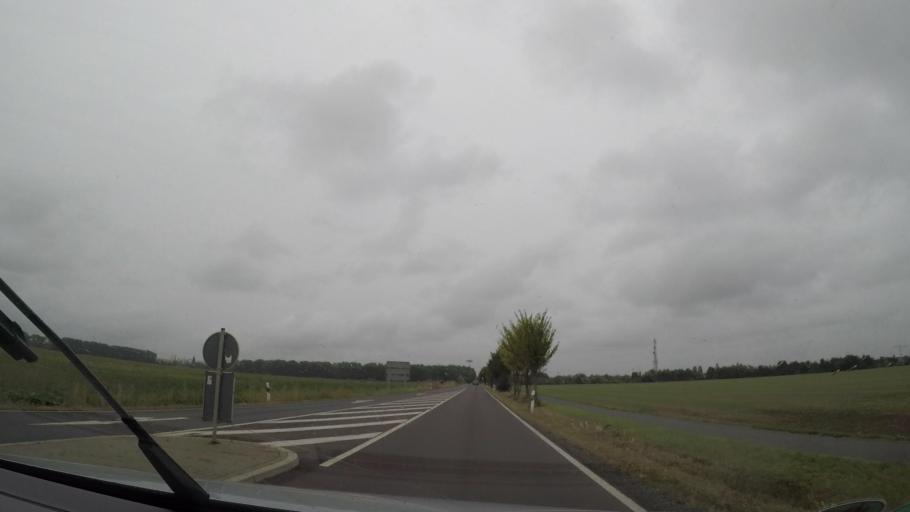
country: DE
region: Saxony-Anhalt
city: Ebendorf
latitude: 52.1722
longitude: 11.5943
